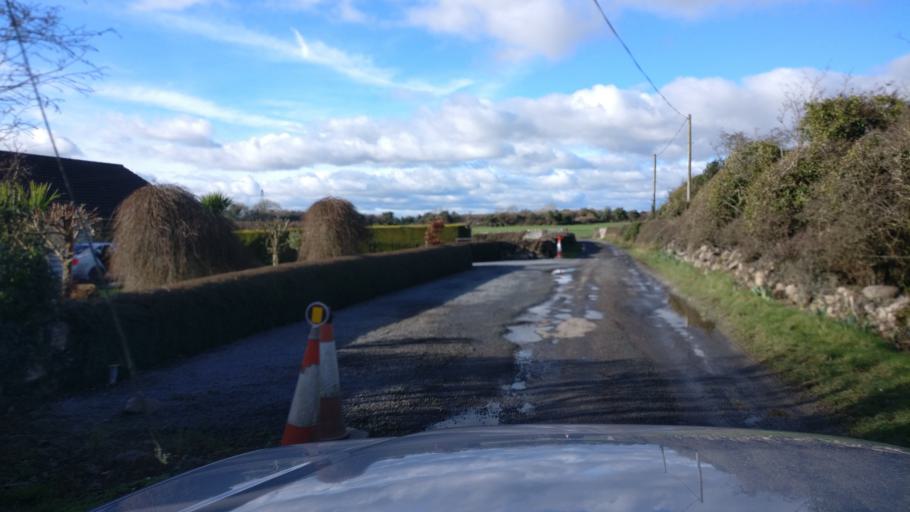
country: IE
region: Connaught
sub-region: County Galway
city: Athenry
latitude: 53.2263
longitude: -8.8108
